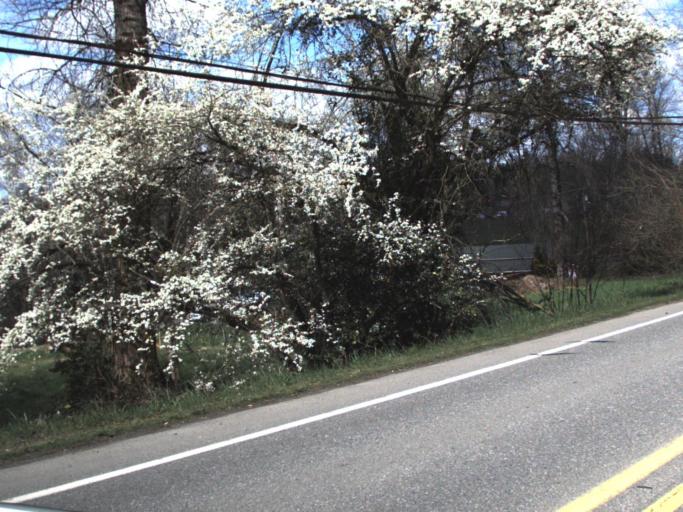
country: US
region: Washington
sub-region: King County
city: Black Diamond
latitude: 47.3155
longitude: -122.0050
